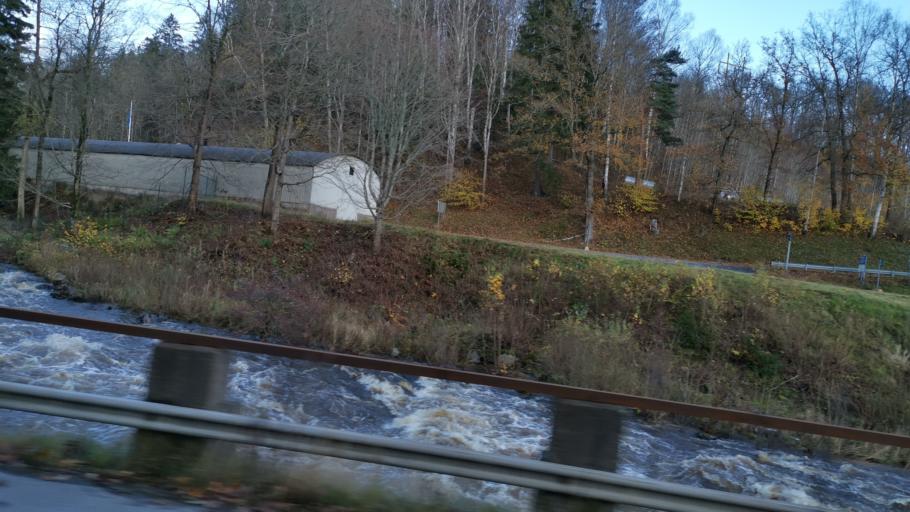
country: SE
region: Vaestra Goetaland
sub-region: Munkedals Kommun
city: Munkedal
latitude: 58.4820
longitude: 11.6925
